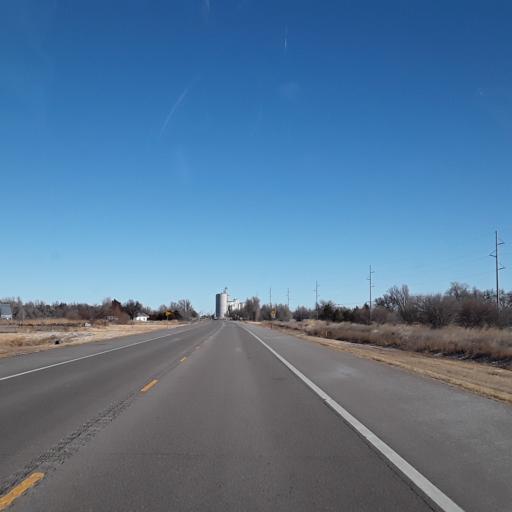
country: US
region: Kansas
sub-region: Pawnee County
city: Larned
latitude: 38.1678
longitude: -99.1101
